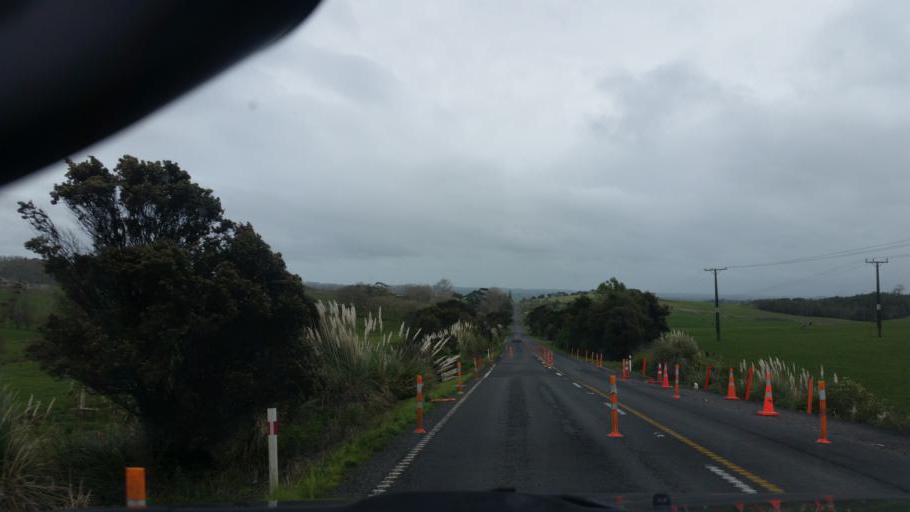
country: NZ
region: Northland
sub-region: Kaipara District
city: Dargaville
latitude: -36.1287
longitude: 174.1326
